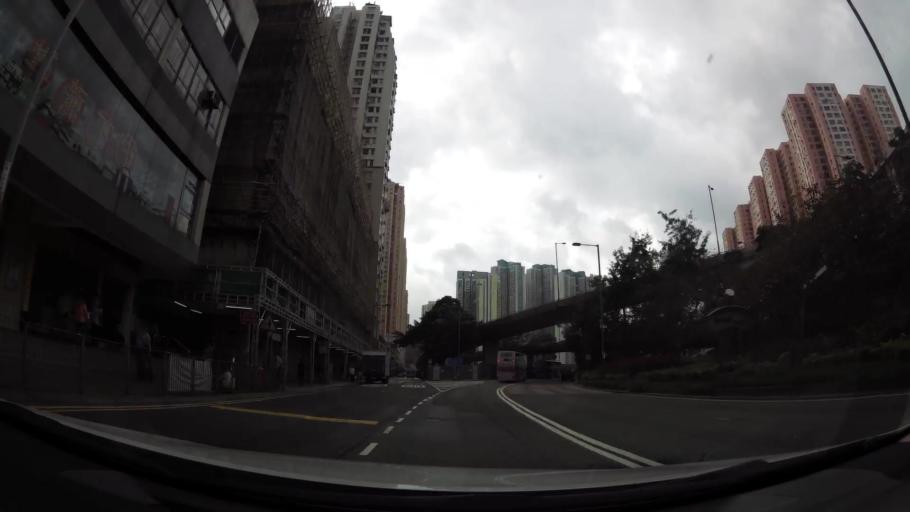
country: HK
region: Kowloon City
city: Kowloon
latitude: 22.3267
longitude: 114.2141
